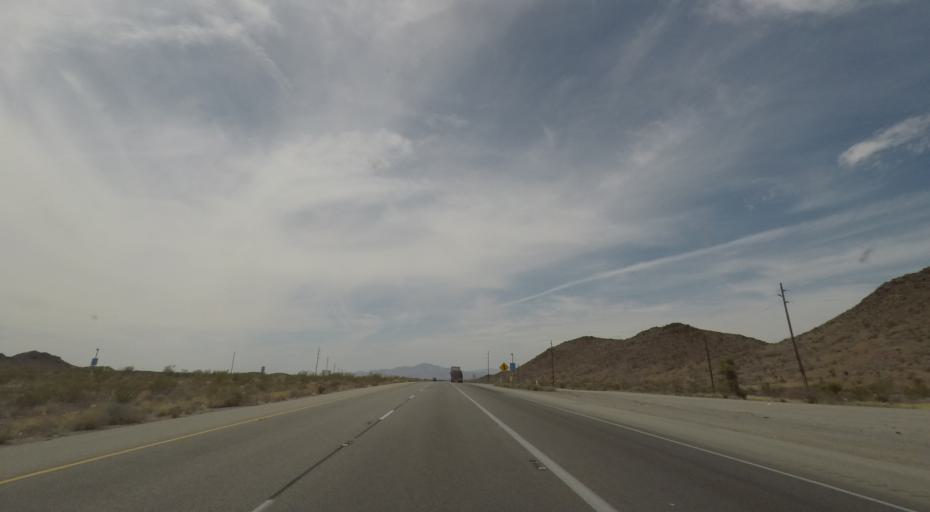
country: US
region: California
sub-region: San Bernardino County
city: Needles
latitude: 34.8299
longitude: -115.0536
